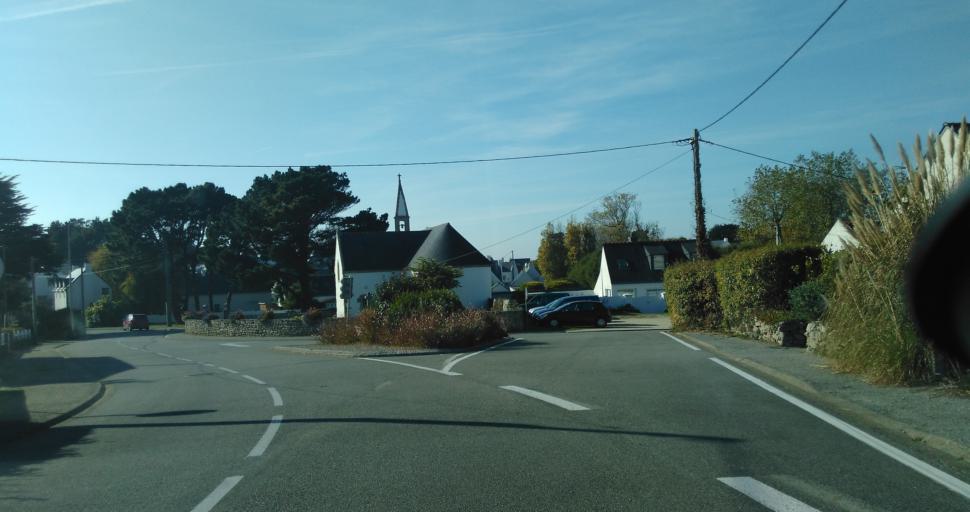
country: FR
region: Brittany
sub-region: Departement du Morbihan
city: Saint-Pierre-Quiberon
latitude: 47.5277
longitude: -3.1430
